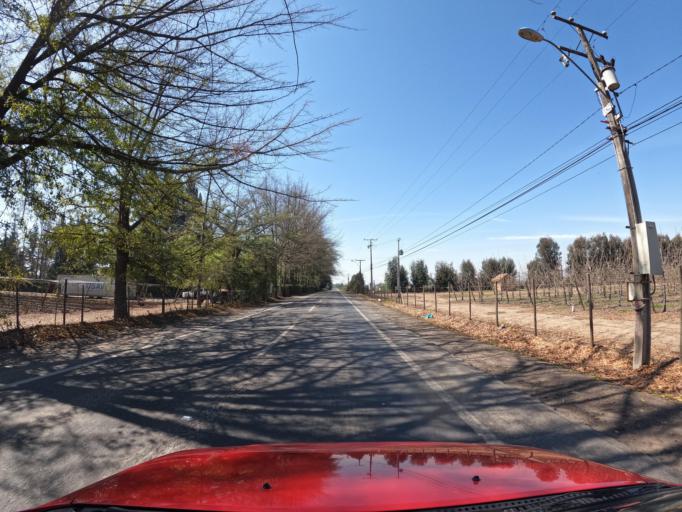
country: CL
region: Maule
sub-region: Provincia de Curico
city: Rauco
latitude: -34.9969
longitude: -71.3669
